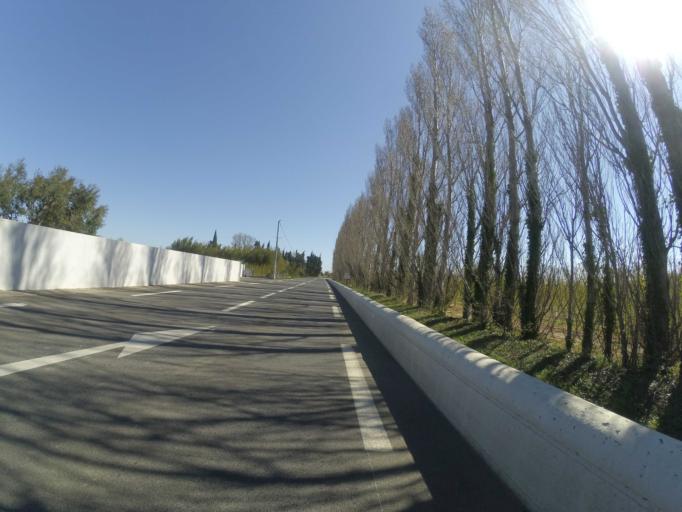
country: FR
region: Languedoc-Roussillon
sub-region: Departement des Pyrenees-Orientales
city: Millas
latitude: 42.6851
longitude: 2.7010
